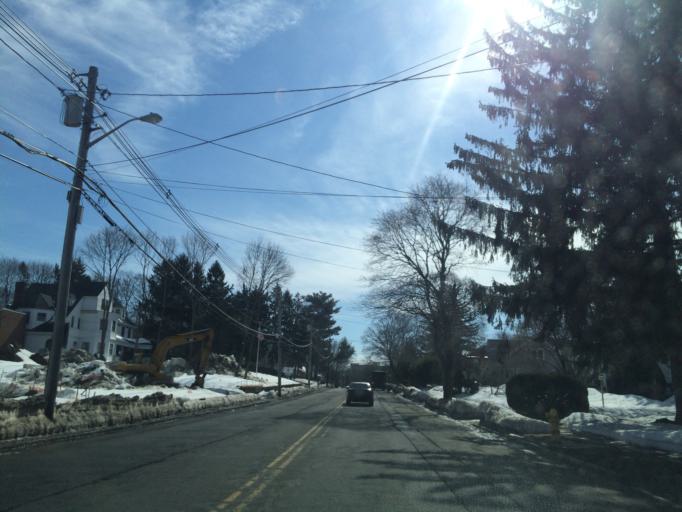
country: US
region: Massachusetts
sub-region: Middlesex County
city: Medford
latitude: 42.4232
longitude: -71.1201
